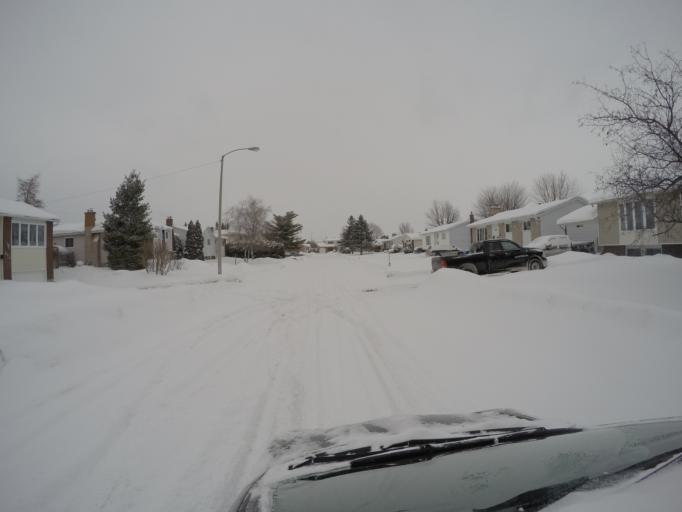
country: CA
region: Quebec
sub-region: Outaouais
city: Gatineau
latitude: 45.4708
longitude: -75.4964
